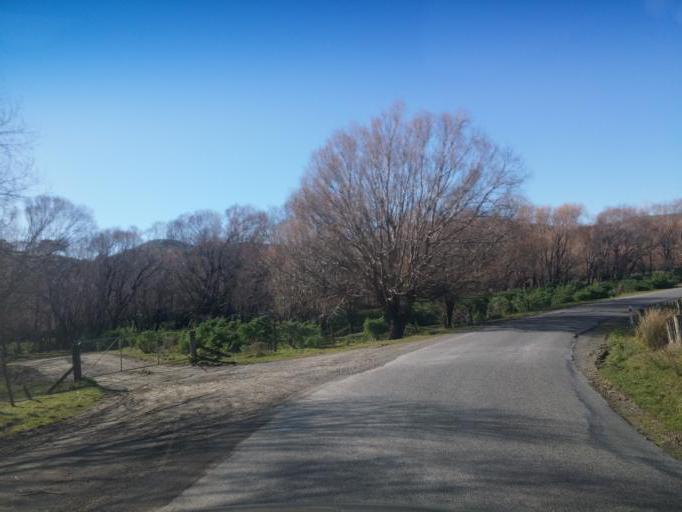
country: NZ
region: Wellington
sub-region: South Wairarapa District
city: Waipawa
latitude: -41.4178
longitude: 175.4923
